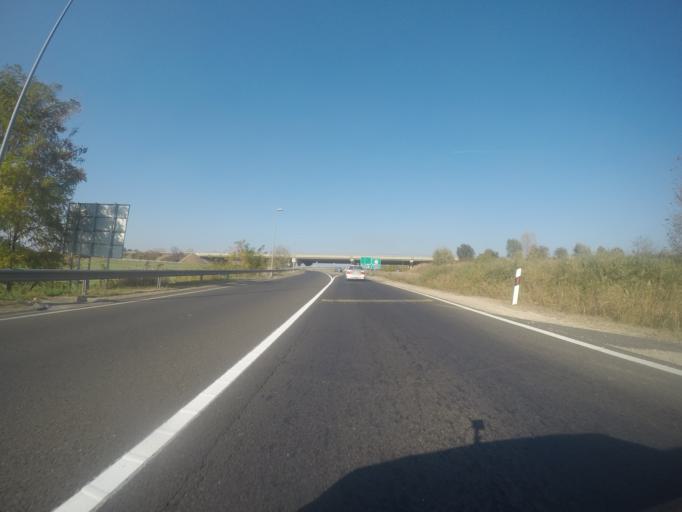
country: HU
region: Fejer
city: Baracs
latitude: 46.9092
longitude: 18.9260
